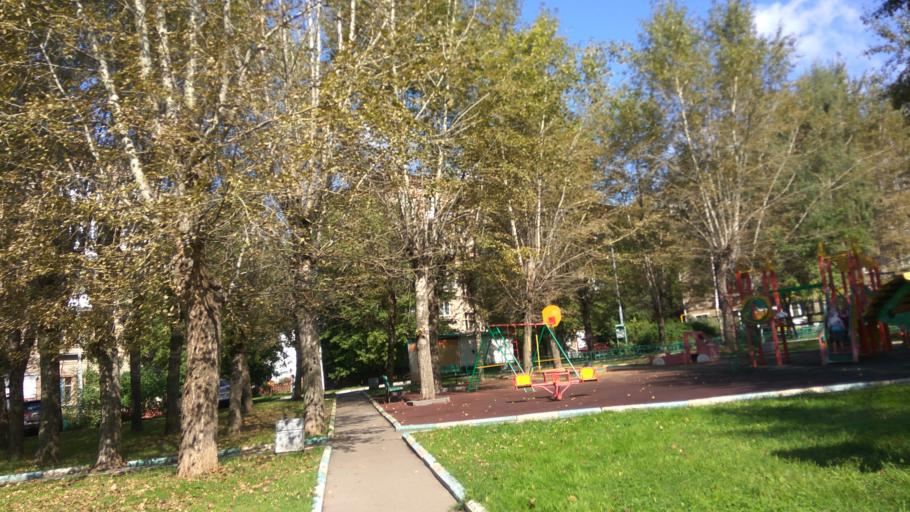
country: RU
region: Moscow
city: Tsaritsyno
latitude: 55.6455
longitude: 37.6651
